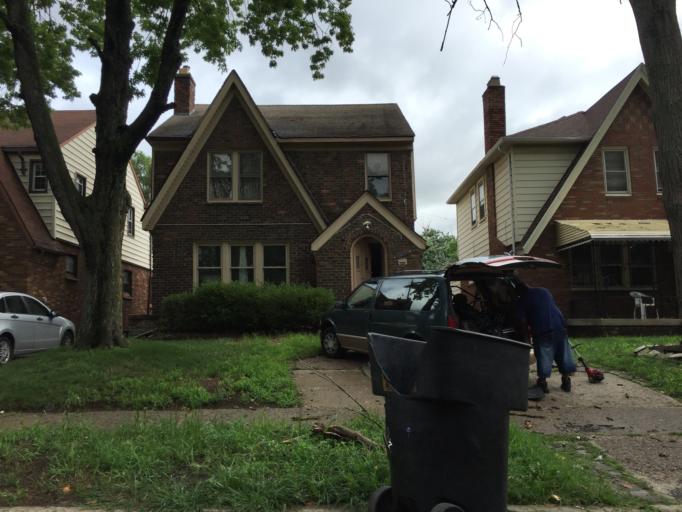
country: US
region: Michigan
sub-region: Oakland County
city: Ferndale
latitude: 42.4108
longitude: -83.1522
